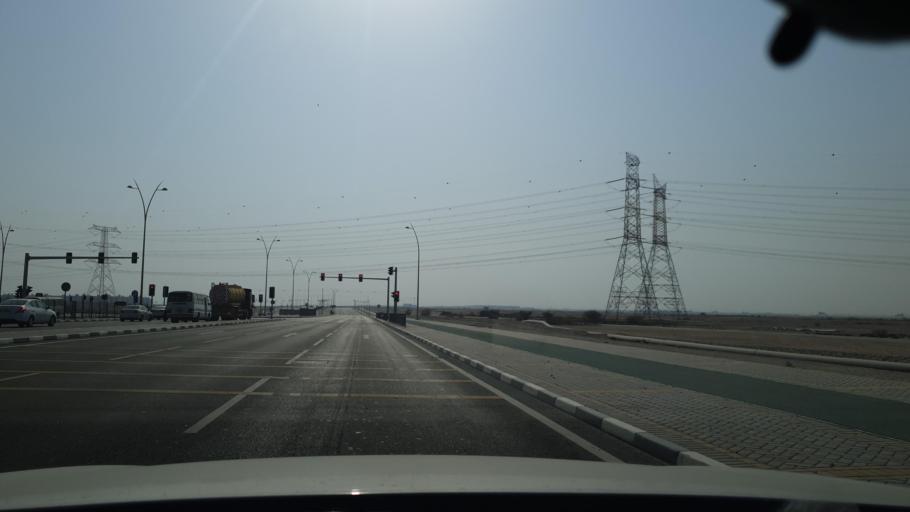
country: QA
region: Al Wakrah
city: Al Wukayr
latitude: 25.1748
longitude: 51.5261
